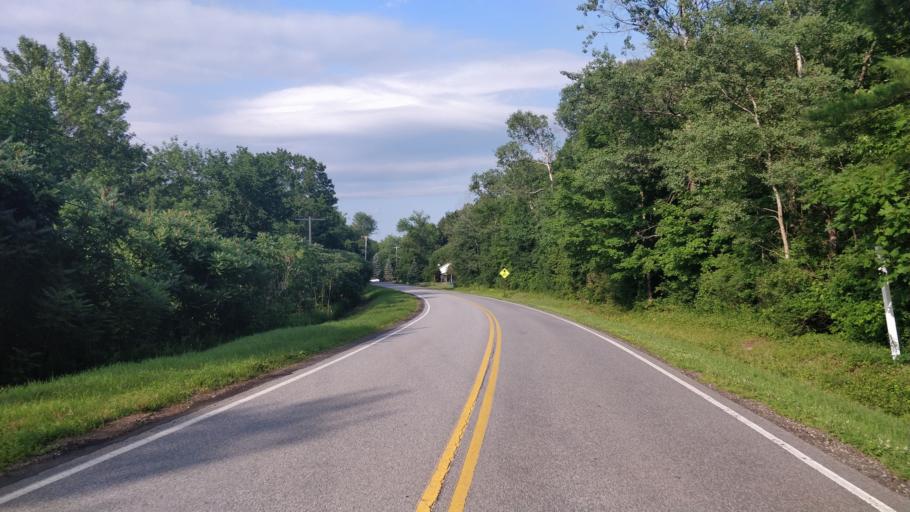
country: US
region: New York
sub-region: Saratoga County
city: North Ballston Spa
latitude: 43.0247
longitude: -73.7988
